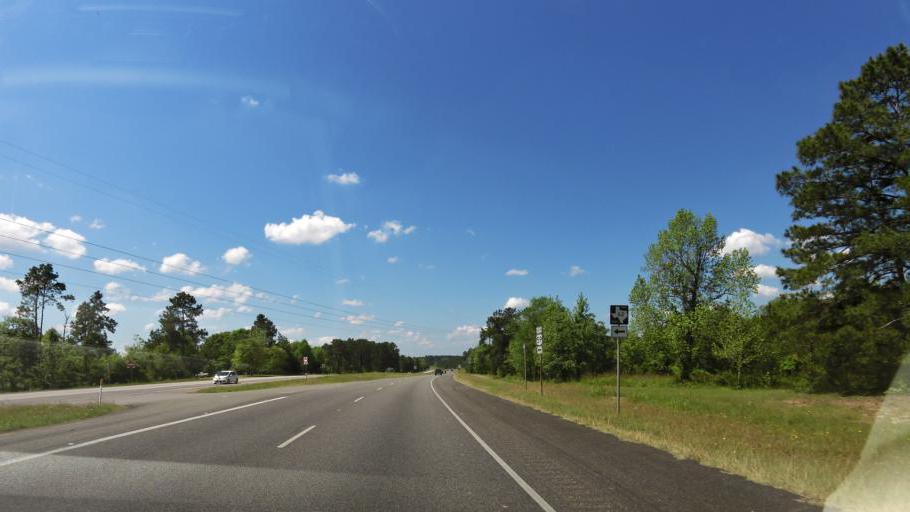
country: US
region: Texas
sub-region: Polk County
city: Corrigan
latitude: 30.9095
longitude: -94.8272
